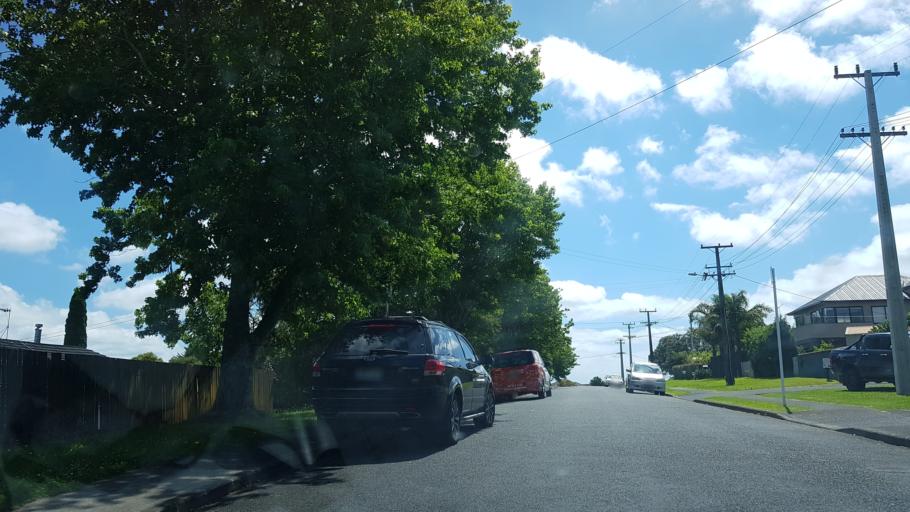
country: NZ
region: Auckland
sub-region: Auckland
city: North Shore
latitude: -36.7907
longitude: 174.7122
